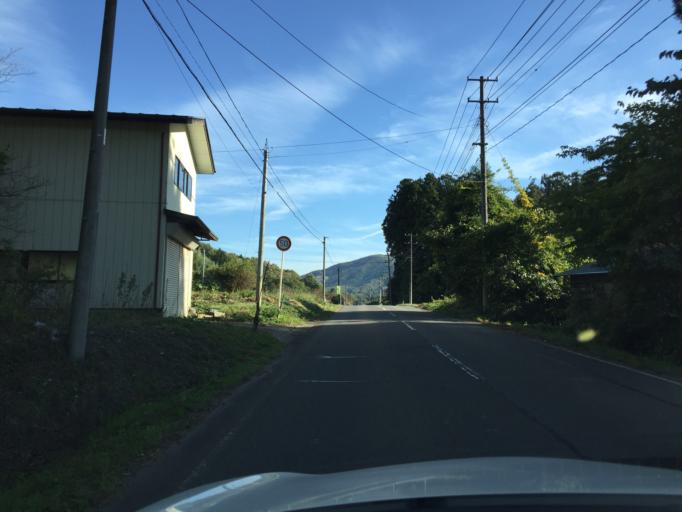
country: JP
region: Fukushima
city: Funehikimachi-funehiki
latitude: 37.3521
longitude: 140.5511
